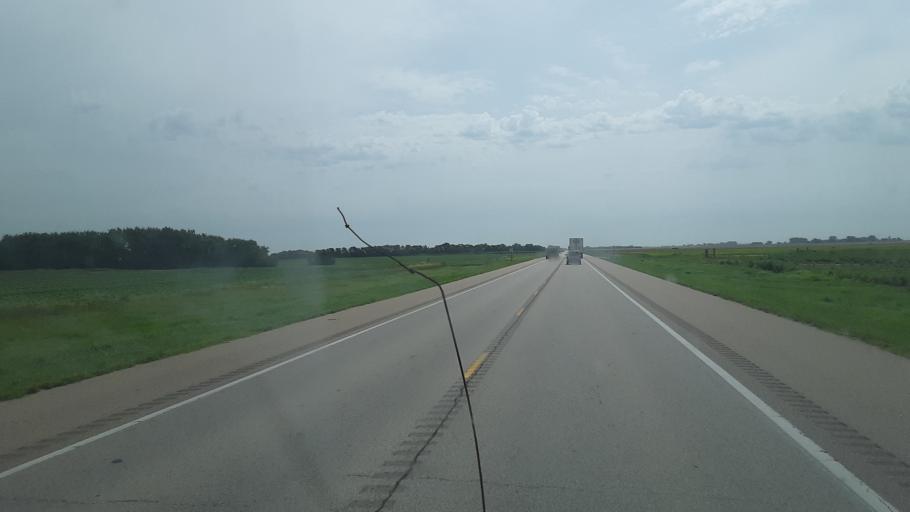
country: US
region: Kansas
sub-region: Reno County
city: Nickerson
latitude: 37.9850
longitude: -98.2178
